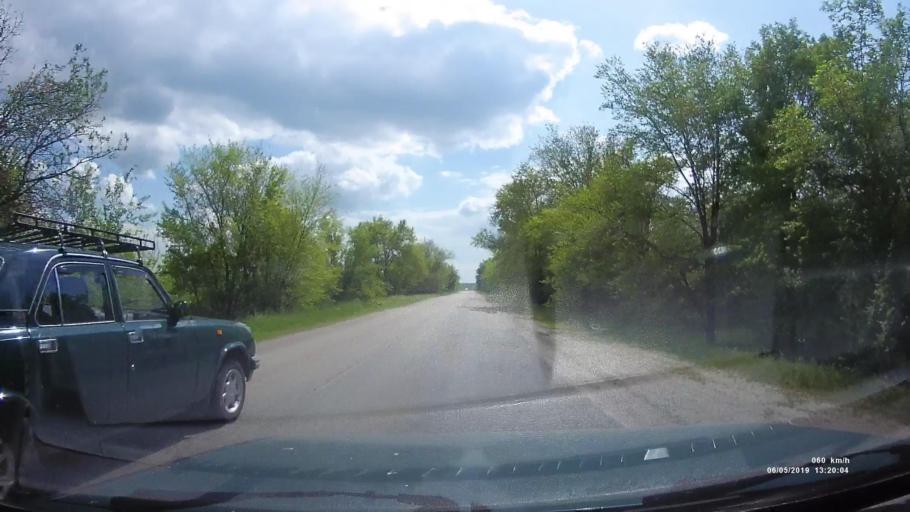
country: RU
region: Rostov
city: Ust'-Donetskiy
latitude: 47.7198
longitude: 40.9119
